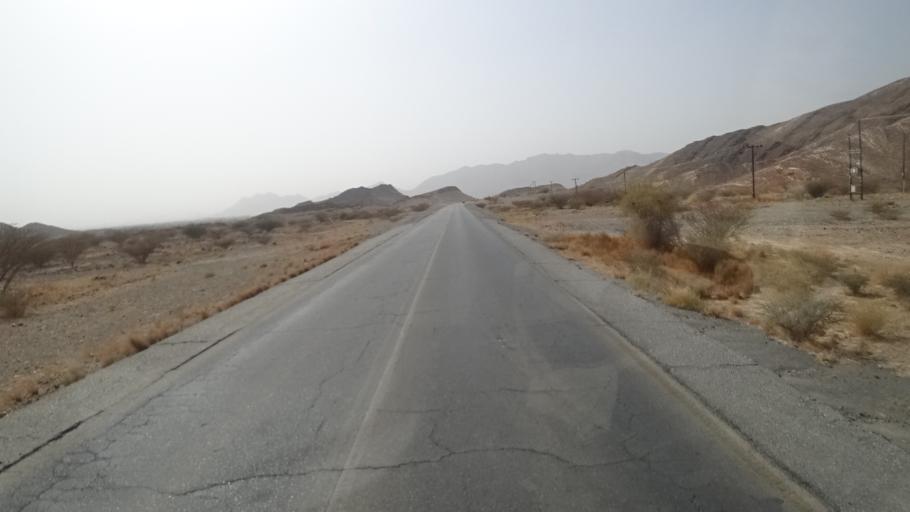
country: OM
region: Muhafazat ad Dakhiliyah
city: Nizwa
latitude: 22.9254
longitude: 57.6384
